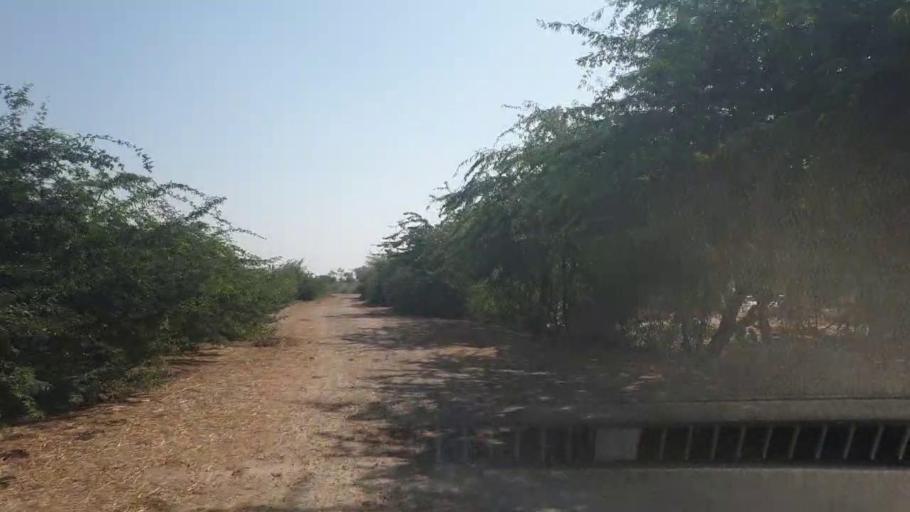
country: PK
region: Sindh
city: Badin
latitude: 24.5458
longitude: 68.8446
